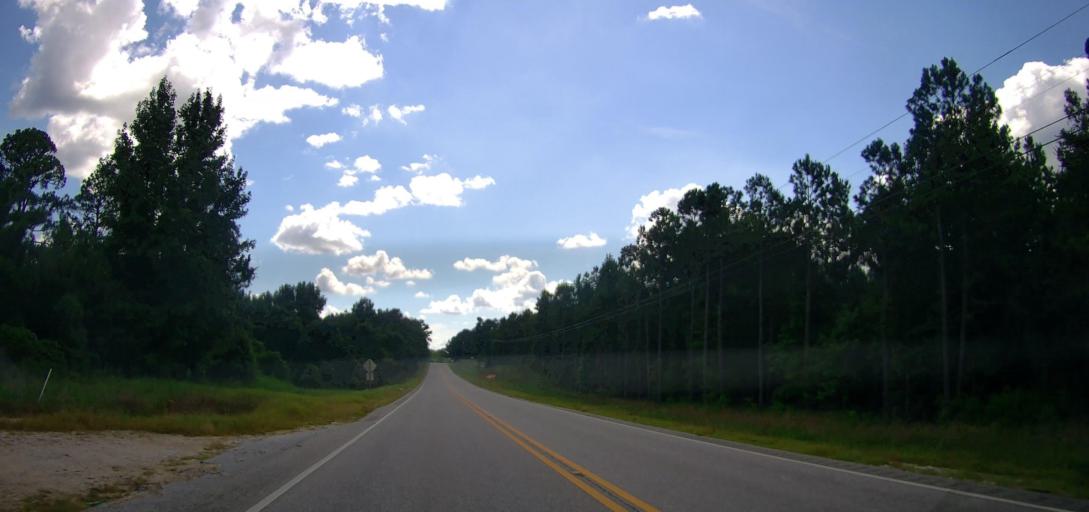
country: US
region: Alabama
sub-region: Macon County
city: Tuskegee
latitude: 32.4636
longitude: -85.6015
